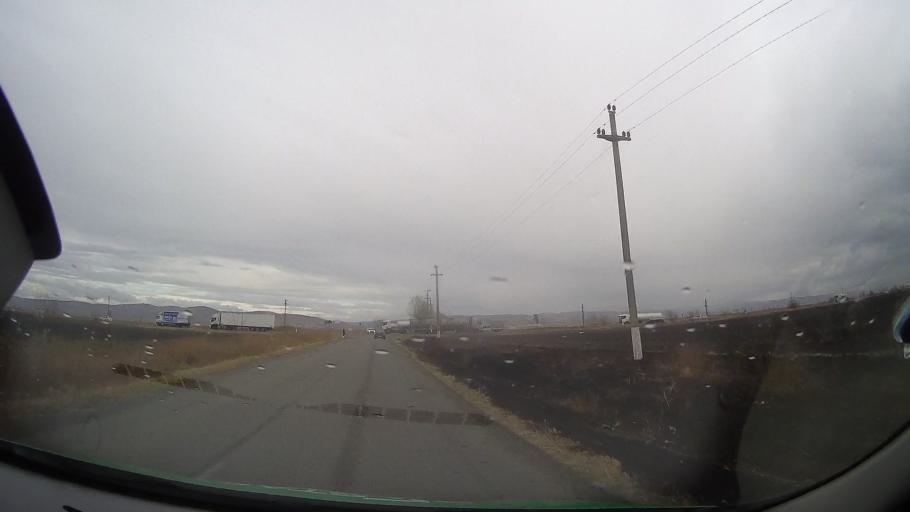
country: RO
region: Prahova
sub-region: Comuna Colceag
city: Inotesti
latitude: 44.9783
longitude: 26.3406
